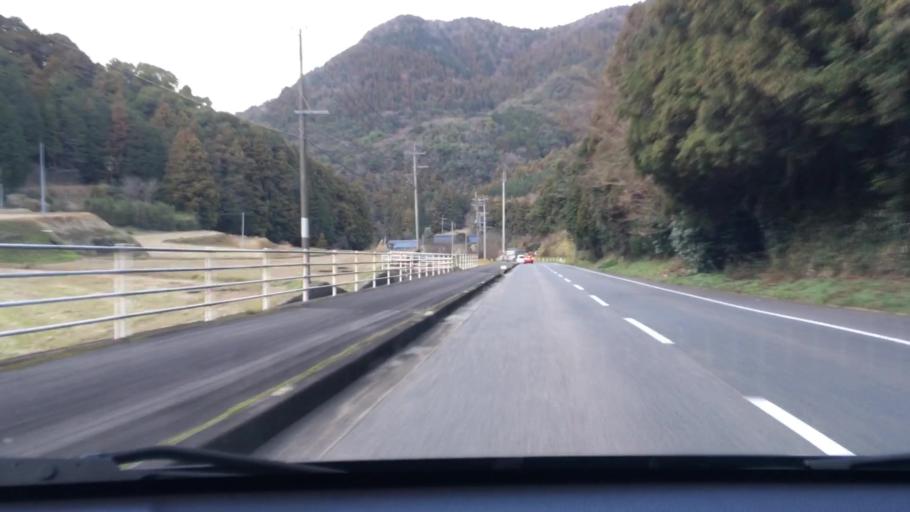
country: JP
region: Oita
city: Bungo-Takada-shi
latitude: 33.4790
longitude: 131.3862
